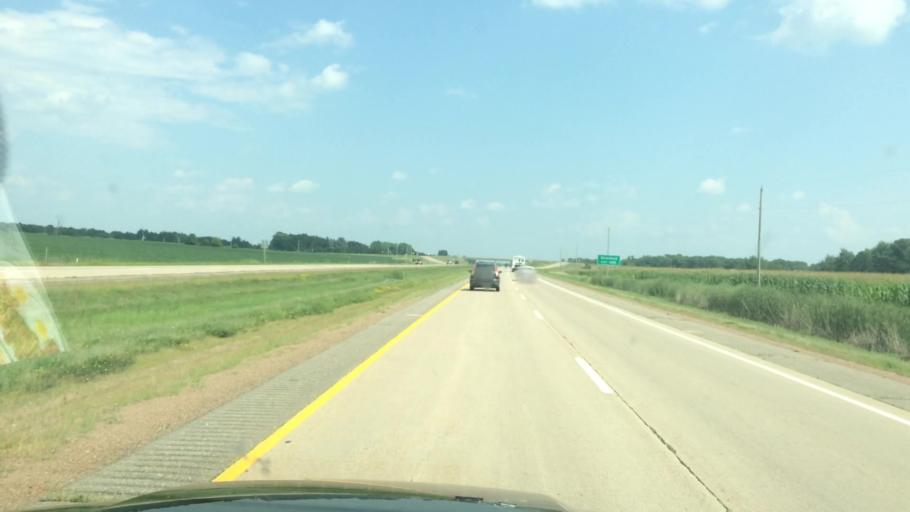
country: US
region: Wisconsin
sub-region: Marathon County
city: Athens
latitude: 44.9451
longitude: -90.0895
